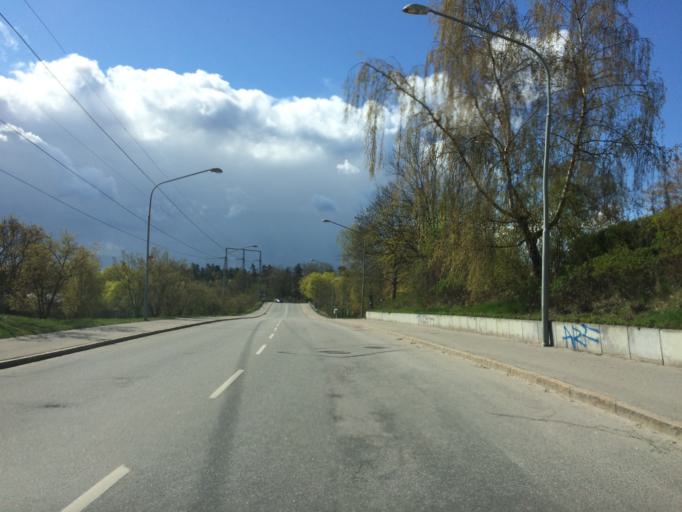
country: SE
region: Stockholm
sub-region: Huddinge Kommun
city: Segeltorp
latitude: 59.2925
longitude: 17.9240
